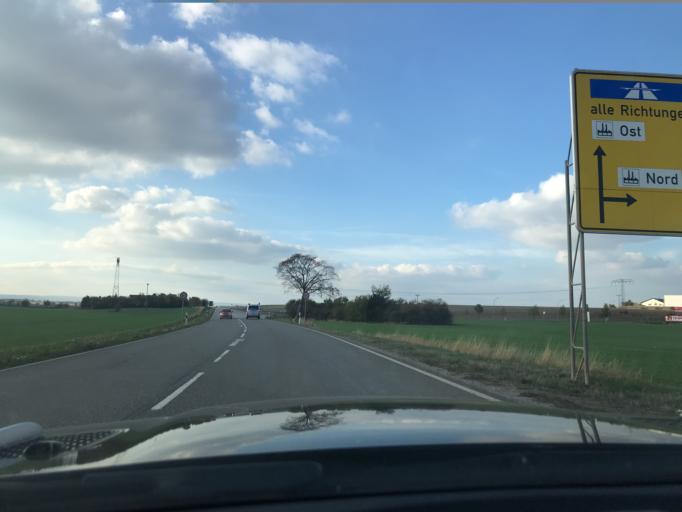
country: DE
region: Thuringia
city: Bad Langensalza
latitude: 51.1163
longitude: 10.6336
